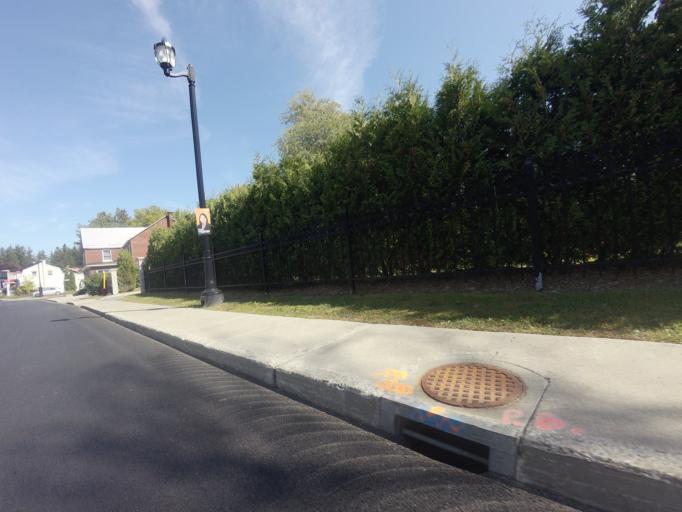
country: CA
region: Quebec
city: Kirkland
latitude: 45.4809
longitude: -73.8699
